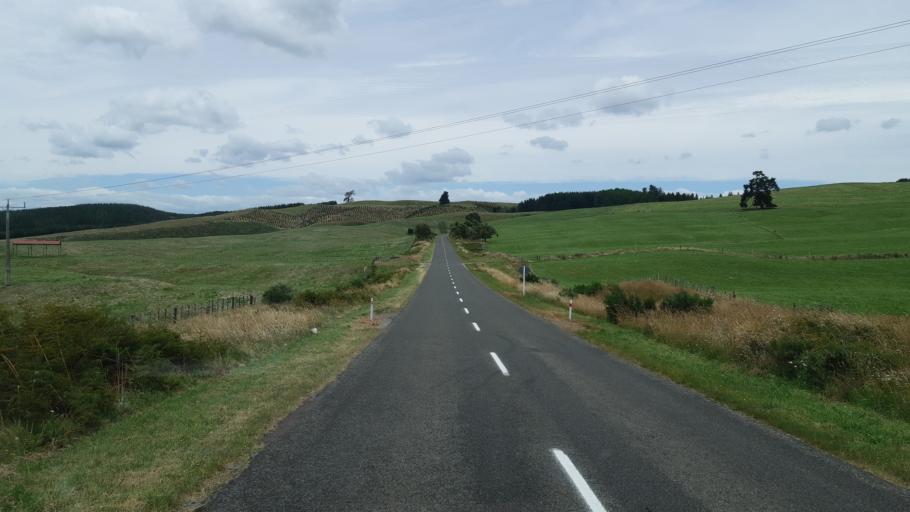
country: NZ
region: Waikato
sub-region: Taupo District
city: Taupo
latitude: -38.6250
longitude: 176.1455
